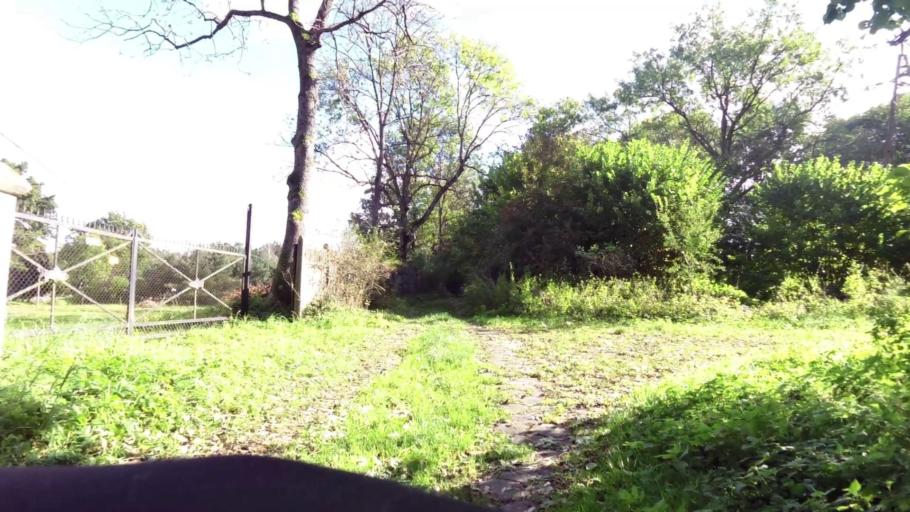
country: PL
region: West Pomeranian Voivodeship
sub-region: Powiat bialogardzki
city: Bialogard
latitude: 53.9883
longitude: 16.0662
